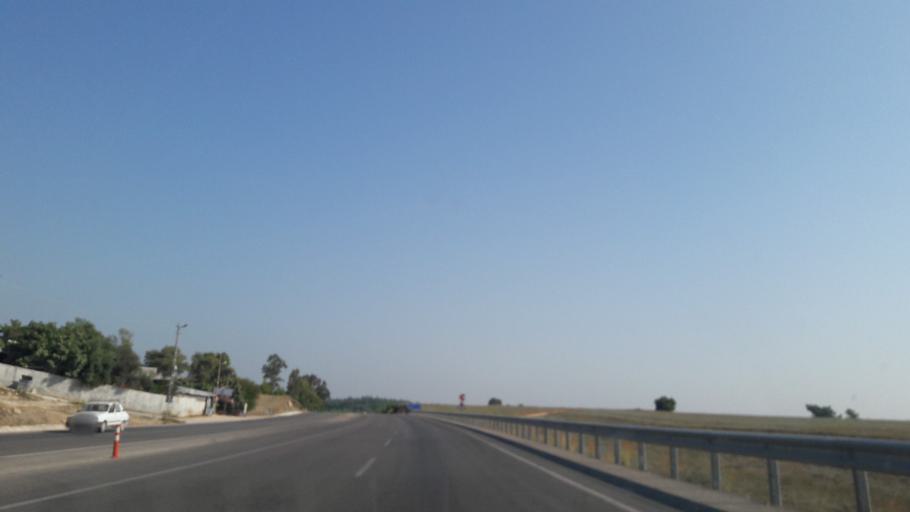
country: TR
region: Adana
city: Sagkaya
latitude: 37.1438
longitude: 35.5404
